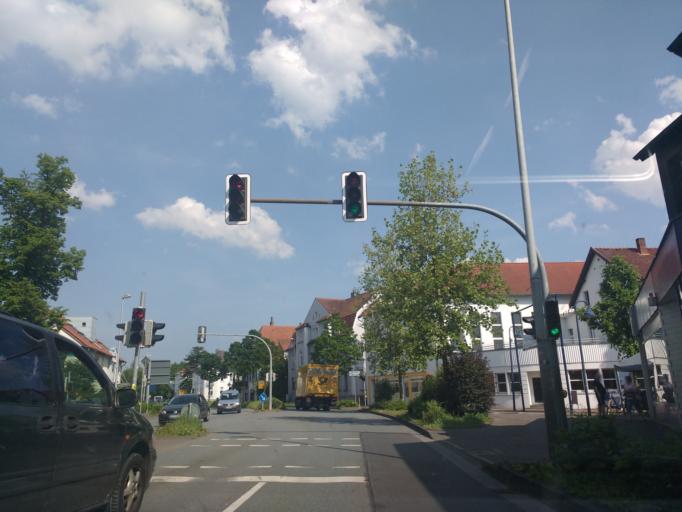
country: DE
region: North Rhine-Westphalia
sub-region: Regierungsbezirk Detmold
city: Lage
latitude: 51.9930
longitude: 8.7927
